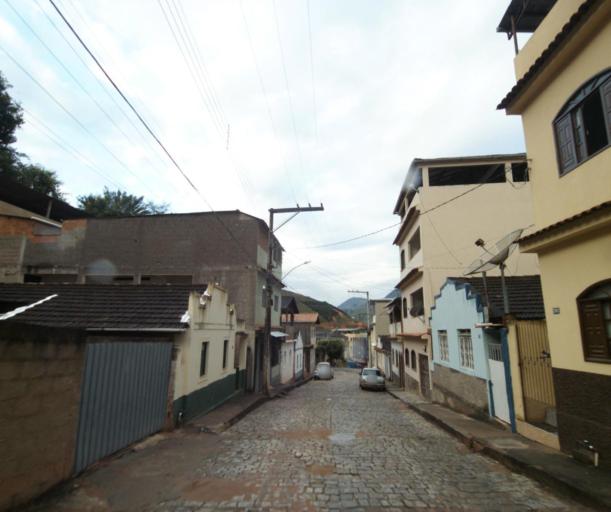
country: BR
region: Espirito Santo
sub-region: Muniz Freire
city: Muniz Freire
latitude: -20.4640
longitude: -41.4157
